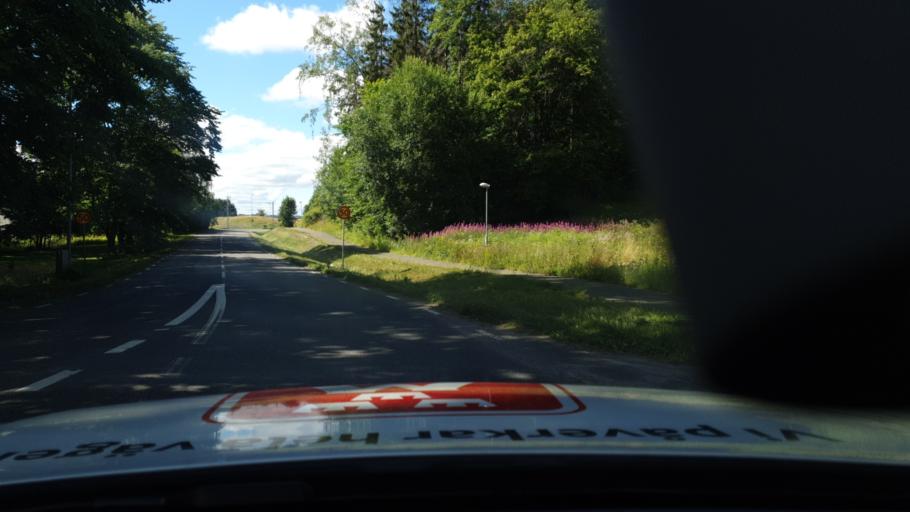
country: SE
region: Vaestra Goetaland
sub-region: Falkopings Kommun
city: Akarp
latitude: 58.2120
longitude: 13.6005
